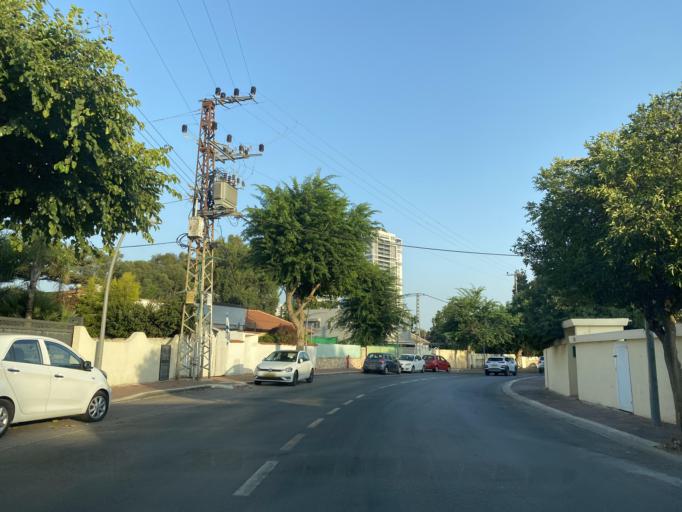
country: IL
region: Tel Aviv
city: Ramat HaSharon
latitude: 32.1354
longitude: 34.8564
